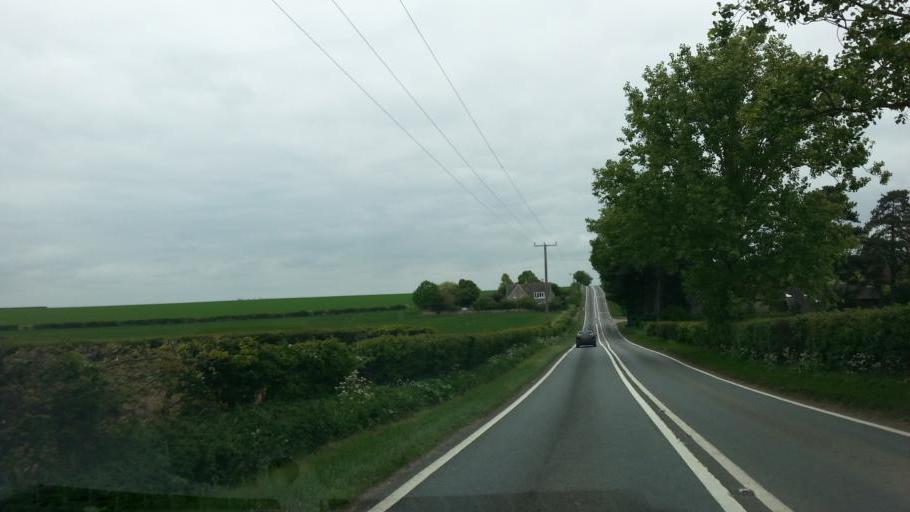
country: GB
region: England
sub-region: Suffolk
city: Bury St Edmunds
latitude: 52.2602
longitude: 0.6767
